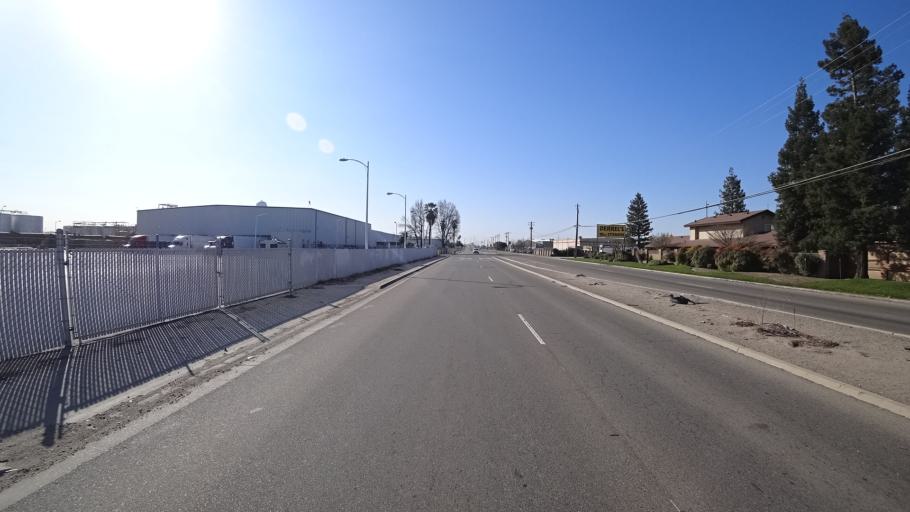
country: US
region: California
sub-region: Fresno County
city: Easton
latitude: 36.6881
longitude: -119.7365
